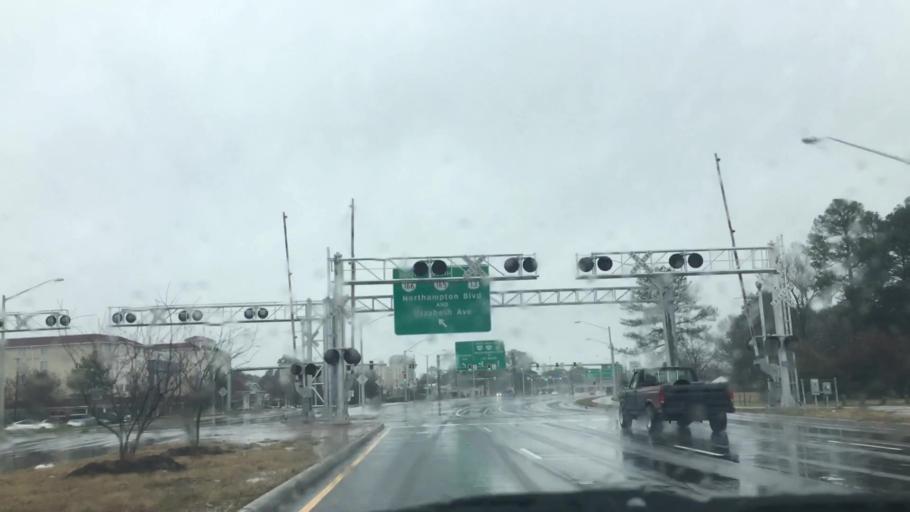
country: US
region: Virginia
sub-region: City of Norfolk
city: Norfolk
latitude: 36.8781
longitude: -76.2115
